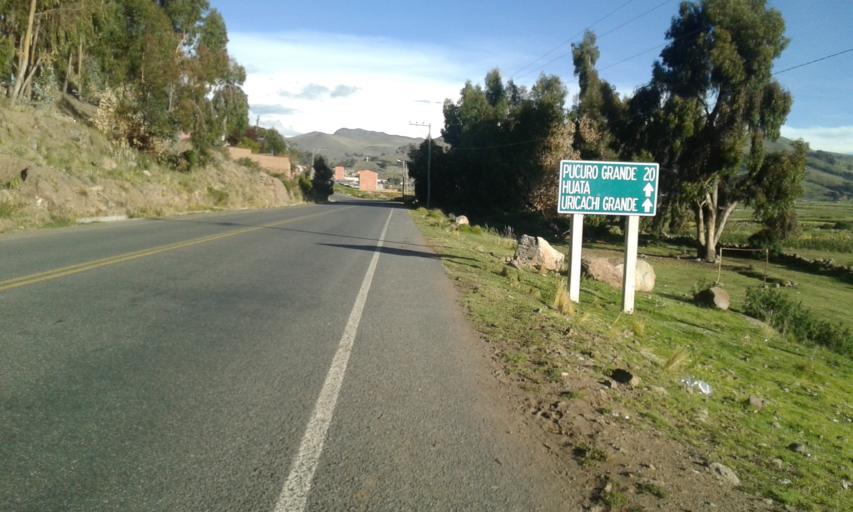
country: BO
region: La Paz
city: Achacachi
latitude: -16.0423
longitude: -68.8343
